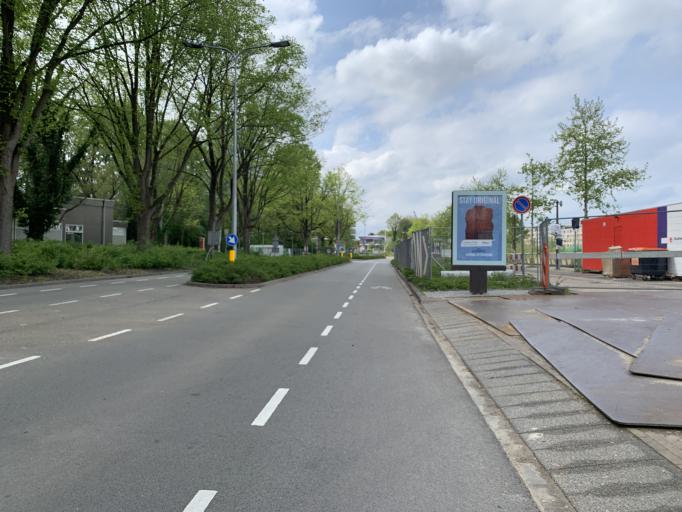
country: NL
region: Groningen
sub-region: Gemeente Groningen
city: Oosterpark
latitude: 53.2043
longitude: 6.5848
